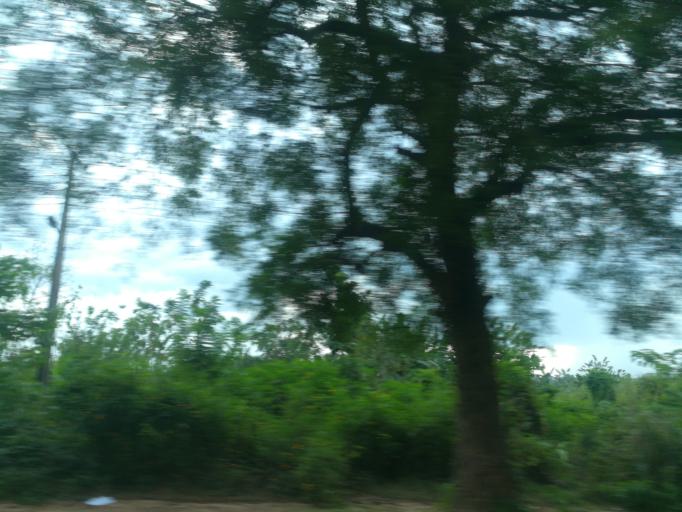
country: NG
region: Oyo
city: Ibadan
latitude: 7.4349
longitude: 3.8874
